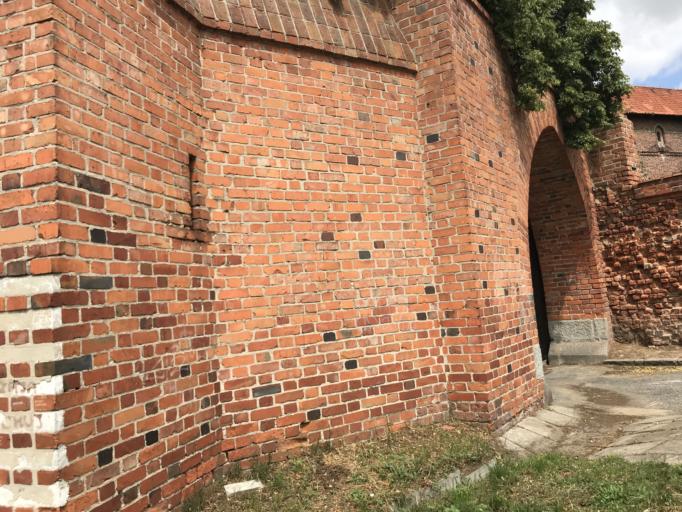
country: PL
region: Pomeranian Voivodeship
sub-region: Powiat malborski
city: Malbork
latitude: 54.0390
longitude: 19.0262
